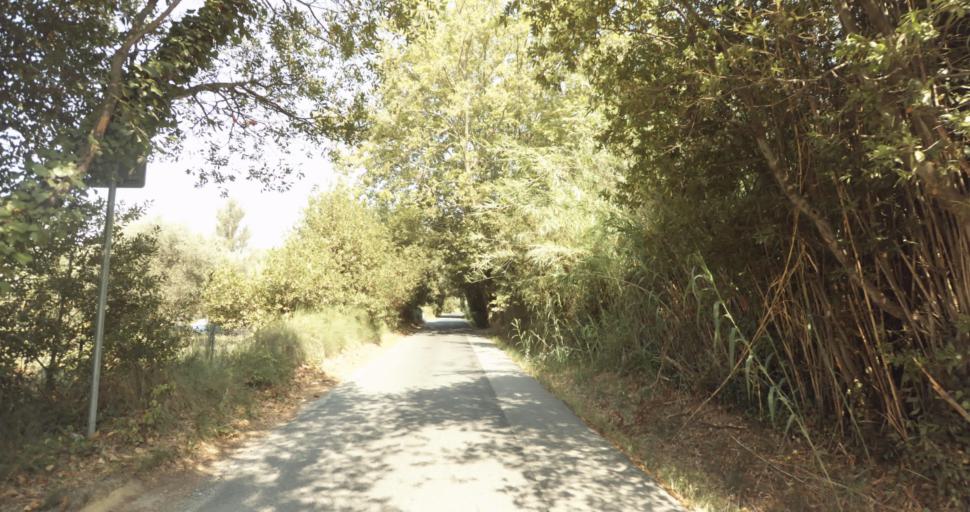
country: FR
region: Languedoc-Roussillon
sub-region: Departement des Pyrenees-Orientales
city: Latour-Bas-Elne
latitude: 42.6150
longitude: 2.9866
